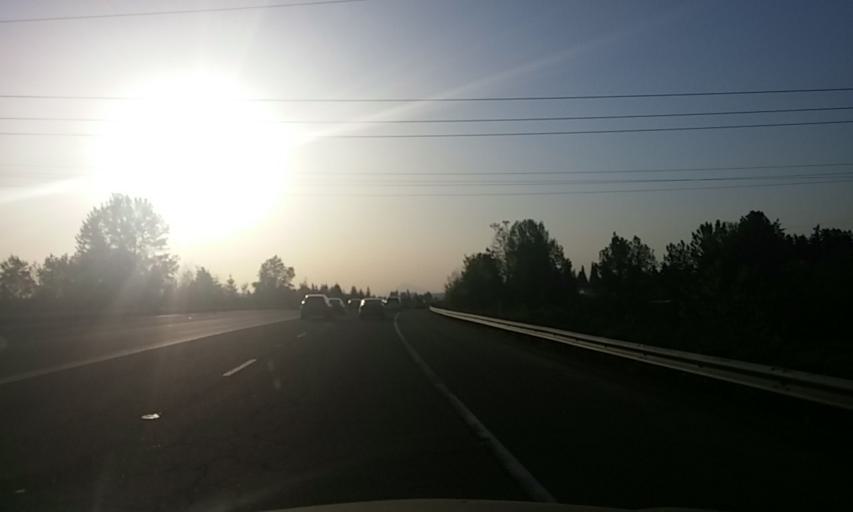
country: US
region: Oregon
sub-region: Washington County
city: Aloha
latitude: 45.4917
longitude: -122.8394
